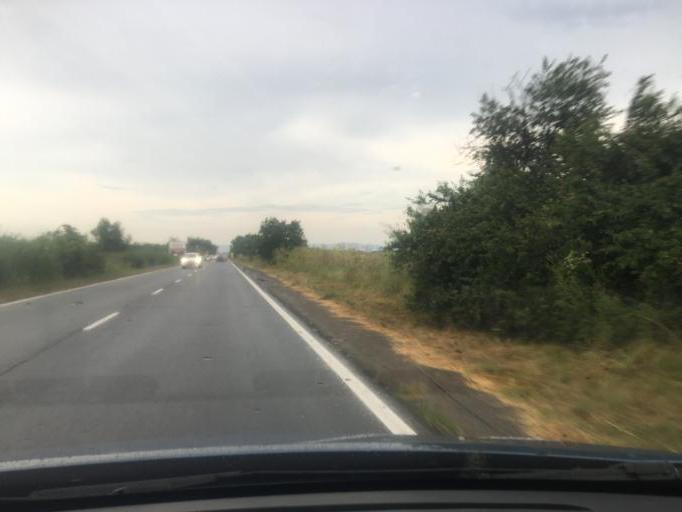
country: BG
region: Burgas
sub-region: Obshtina Pomorie
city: Pomorie
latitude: 42.5898
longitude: 27.6118
